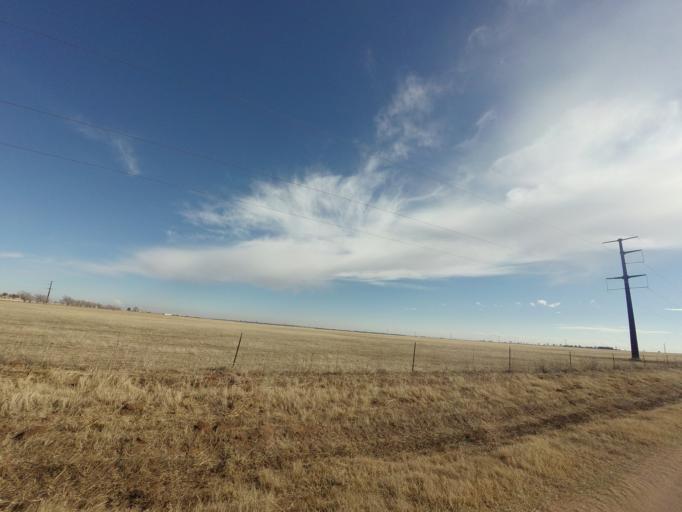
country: US
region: New Mexico
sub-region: Curry County
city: Texico
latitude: 34.4036
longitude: -103.1258
